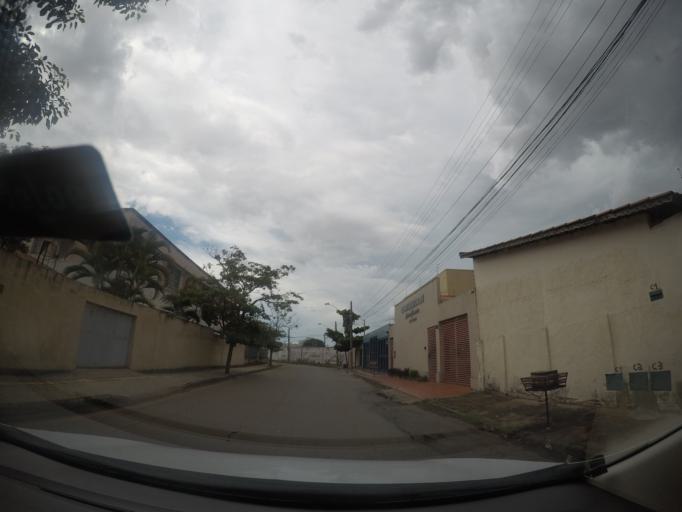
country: BR
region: Goias
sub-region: Goiania
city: Goiania
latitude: -16.6796
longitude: -49.2870
